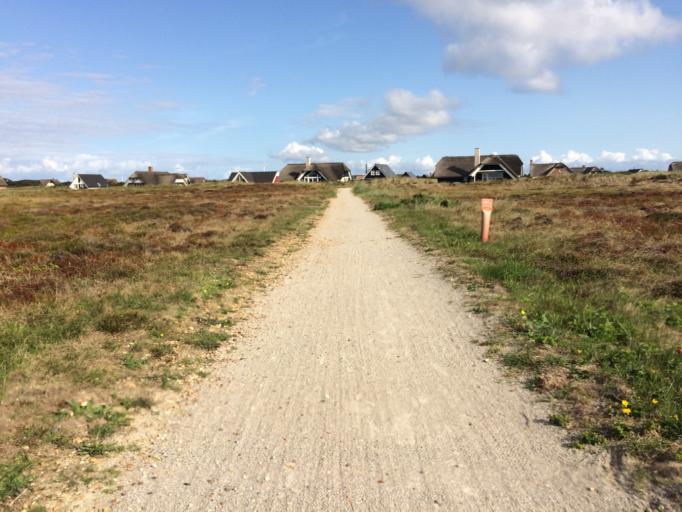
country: DK
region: Central Jutland
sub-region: Ringkobing-Skjern Kommune
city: Hvide Sande
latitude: 55.8848
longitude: 8.1685
